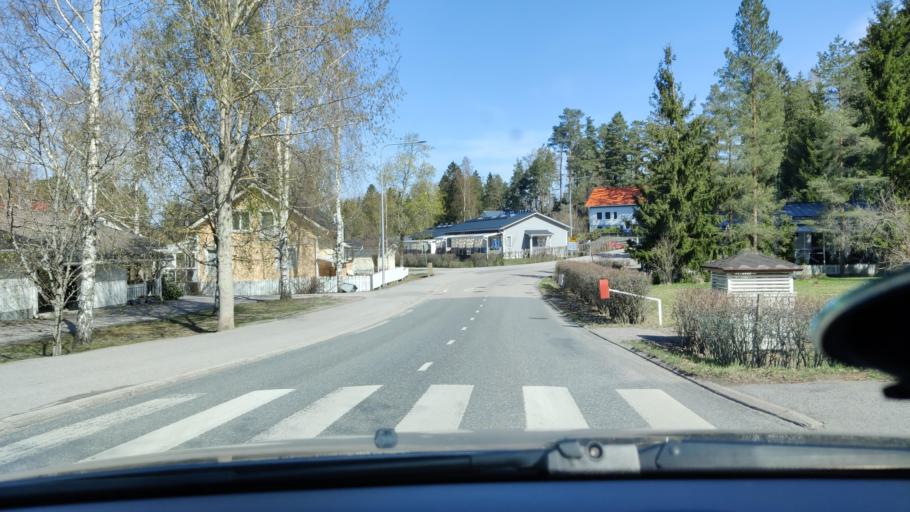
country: FI
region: Uusimaa
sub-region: Helsinki
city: Kerava
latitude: 60.3595
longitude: 25.0902
